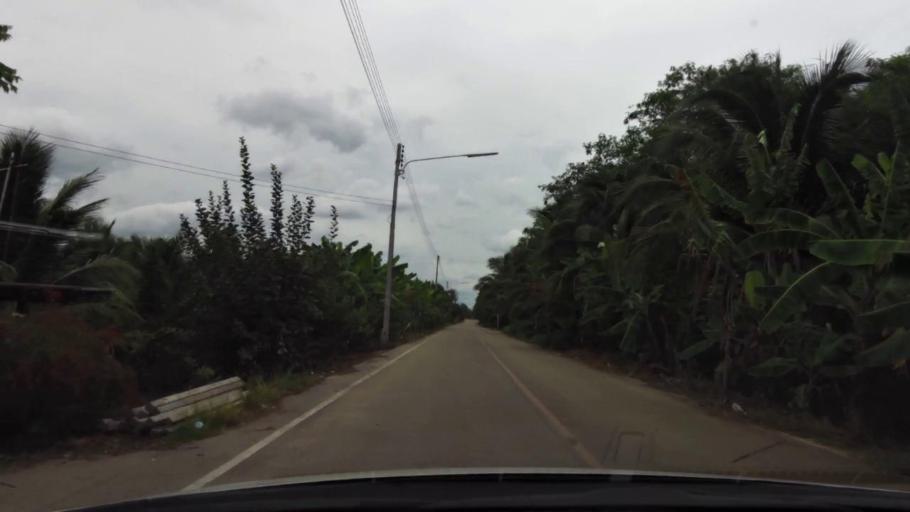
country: TH
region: Ratchaburi
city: Damnoen Saduak
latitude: 13.5506
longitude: 100.0222
